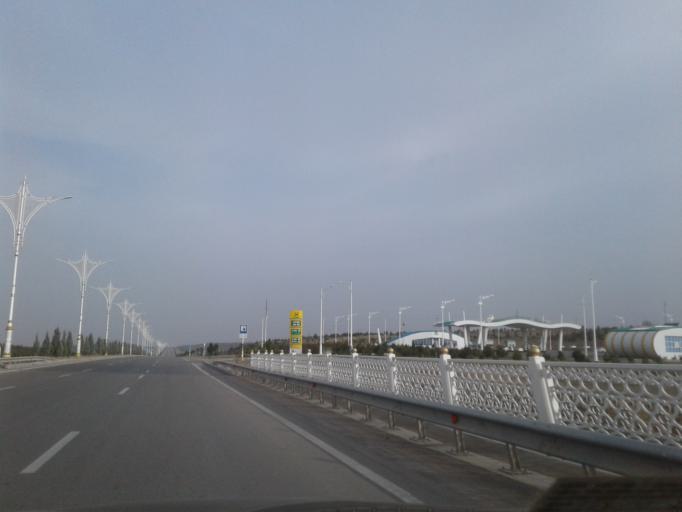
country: TM
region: Ahal
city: Ashgabat
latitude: 37.8778
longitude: 58.4282
